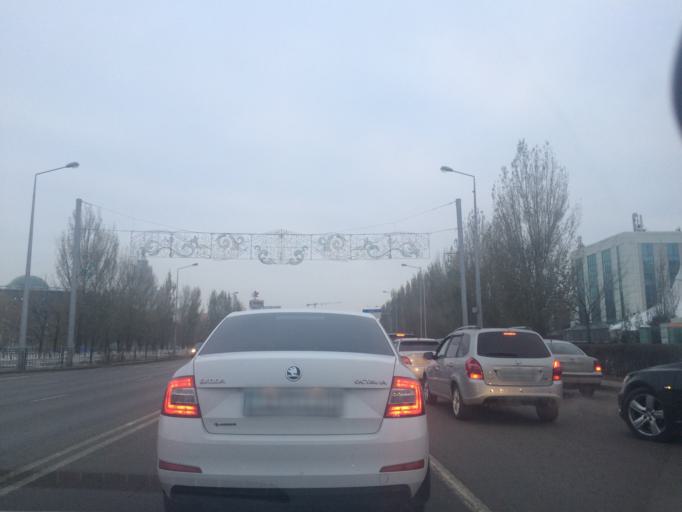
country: KZ
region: Astana Qalasy
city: Astana
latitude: 51.1484
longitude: 71.4124
